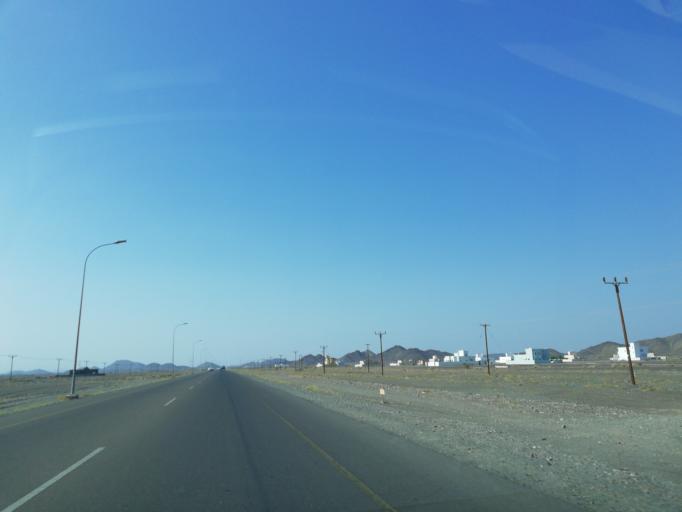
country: OM
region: Ash Sharqiyah
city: Ibra'
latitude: 22.7659
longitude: 58.1449
